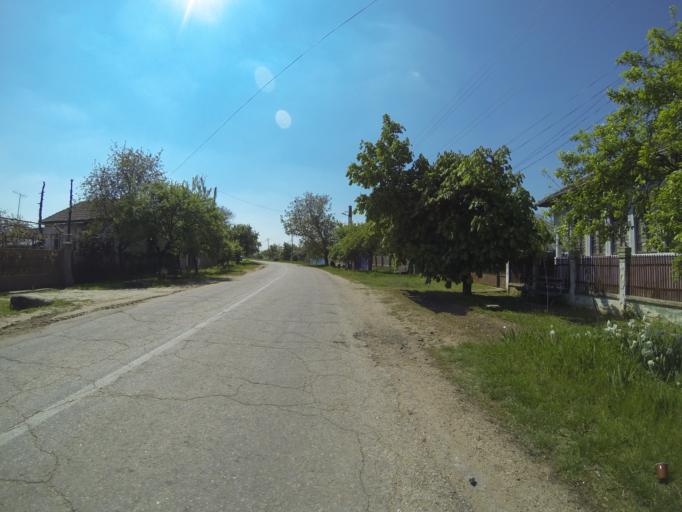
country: RO
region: Dolj
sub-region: Comuna Caraula
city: Caraula
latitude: 44.1952
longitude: 23.2445
